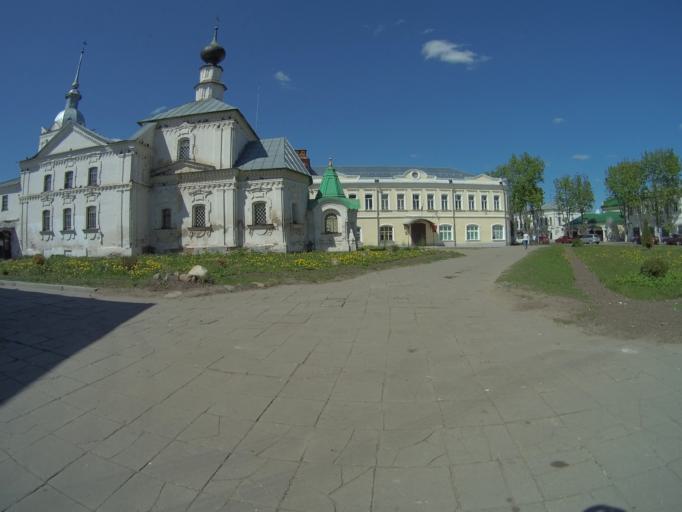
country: RU
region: Vladimir
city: Suzdal'
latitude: 56.4209
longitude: 40.4484
